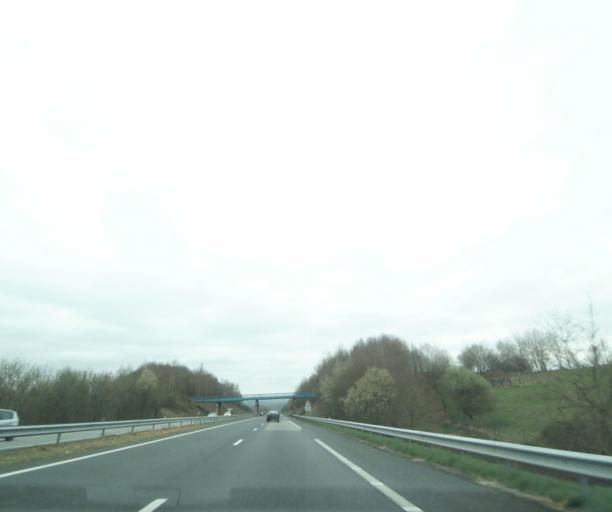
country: FR
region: Limousin
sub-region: Departement de la Correze
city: Uzerche
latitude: 45.4444
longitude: 1.5098
